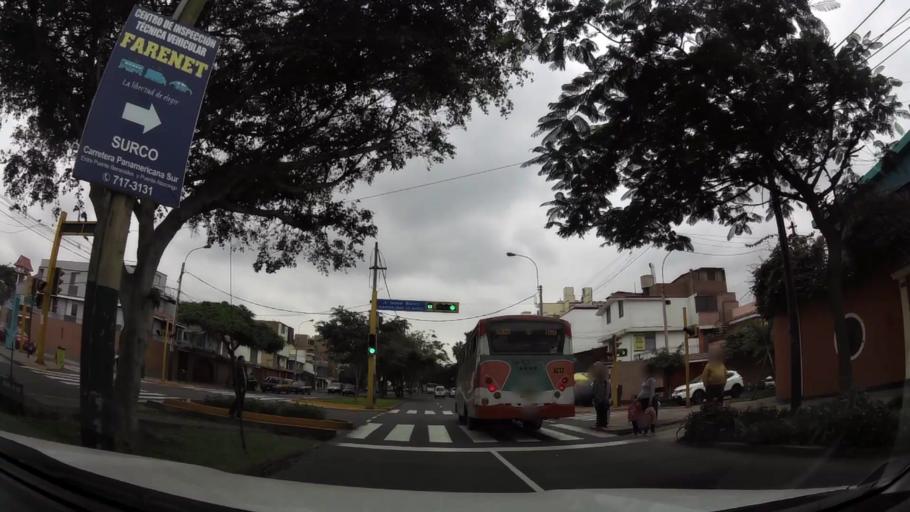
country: PE
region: Lima
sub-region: Lima
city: Surco
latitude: -12.1358
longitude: -76.9838
